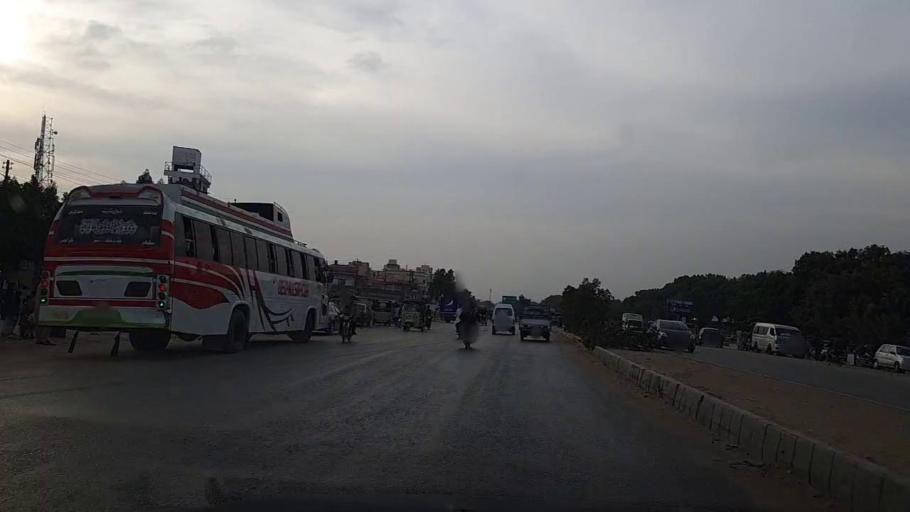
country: PK
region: Sindh
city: Malir Cantonment
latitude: 24.8598
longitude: 67.3369
